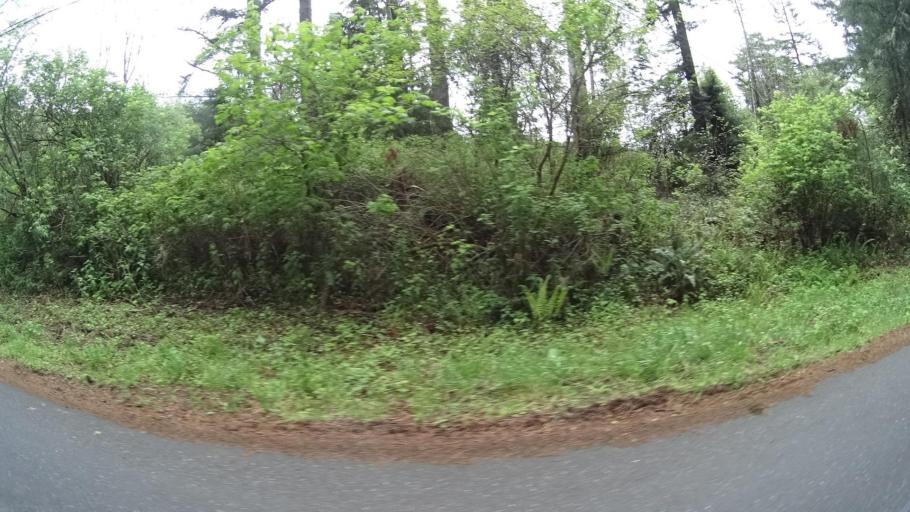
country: US
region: California
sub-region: Humboldt County
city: Bayside
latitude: 40.8306
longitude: -124.0123
